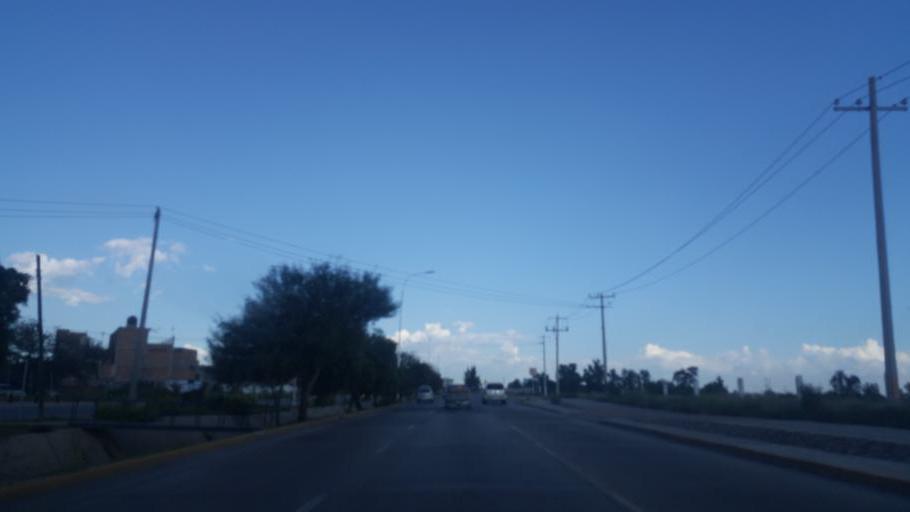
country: MX
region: Guanajuato
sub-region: Leon
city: San Jose de Duran (Los Troncoso)
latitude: 21.0779
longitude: -101.6548
